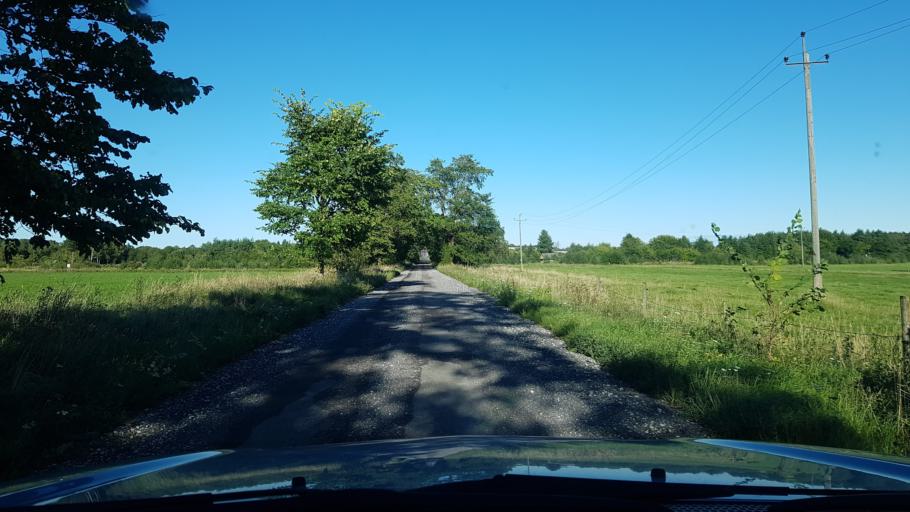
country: EE
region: Harju
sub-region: Tallinna linn
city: Kose
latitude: 59.4101
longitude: 24.8894
